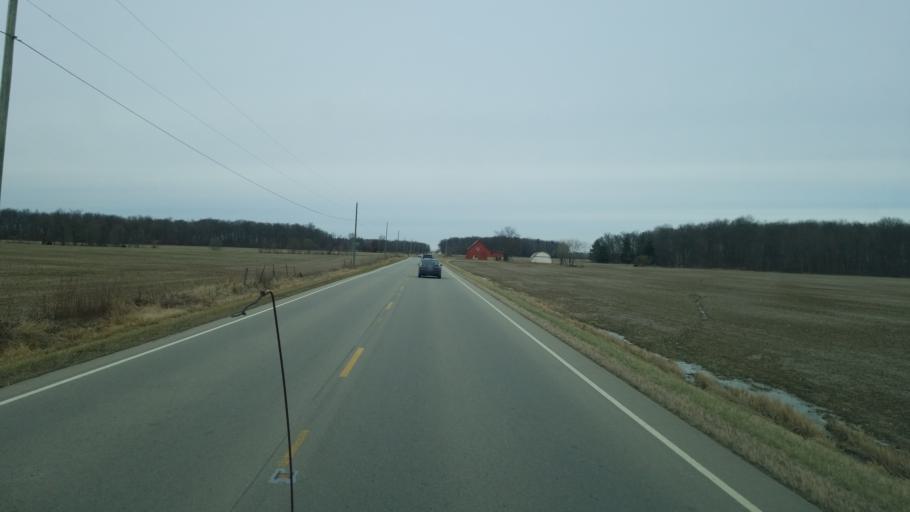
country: US
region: Ohio
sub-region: Adams County
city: Winchester
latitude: 39.0454
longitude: -83.7041
